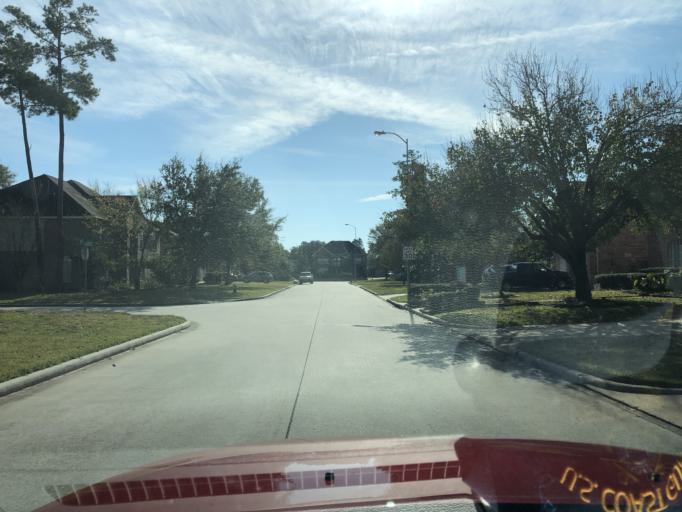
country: US
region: Texas
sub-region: Harris County
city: Tomball
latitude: 30.0264
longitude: -95.5601
